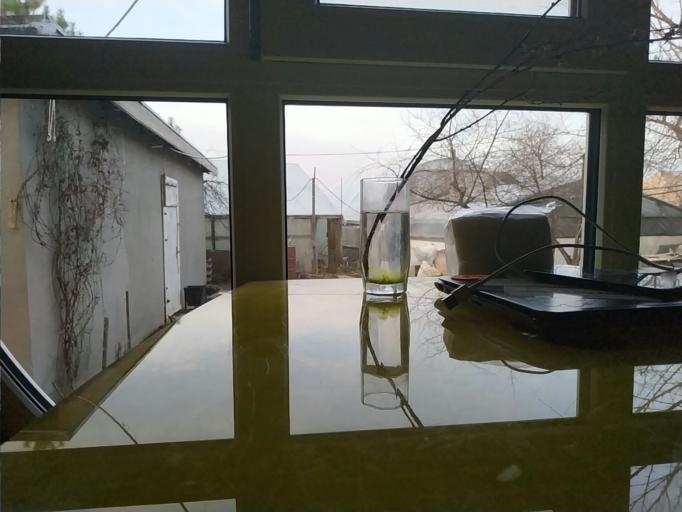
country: RU
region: Republic of Karelia
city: Suoyarvi
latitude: 62.4332
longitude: 32.0117
